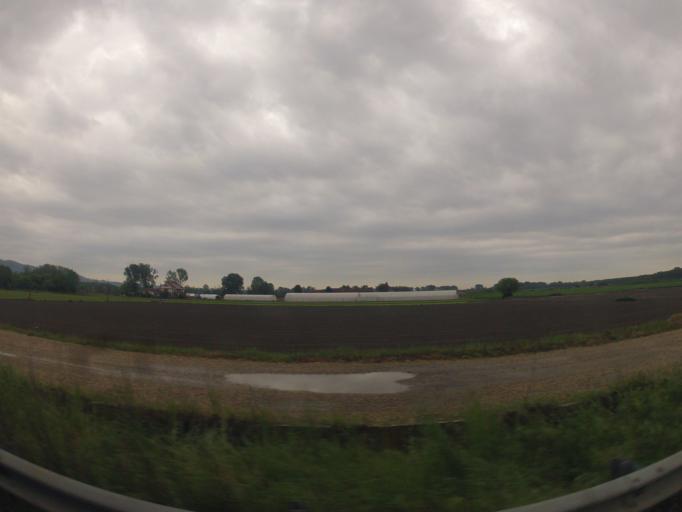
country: IT
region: Piedmont
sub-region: Provincia di Torino
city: La Loggia
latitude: 44.9591
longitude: 7.6805
